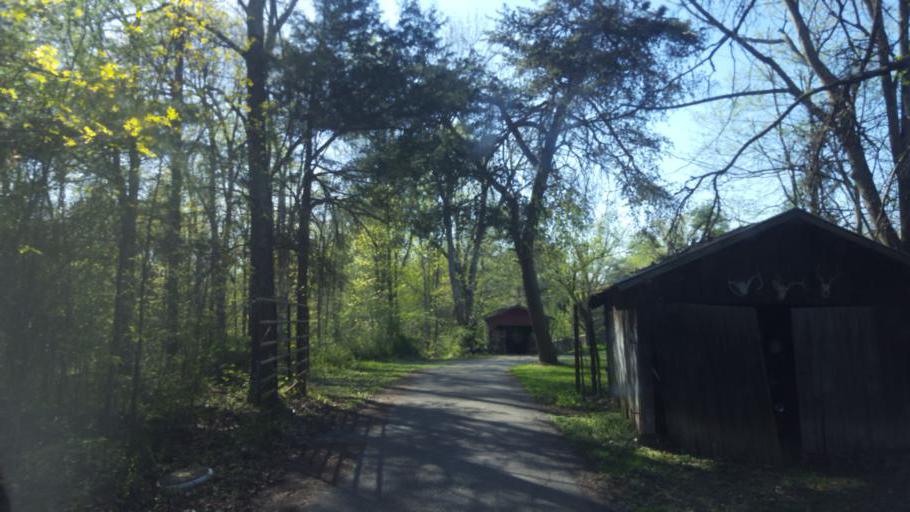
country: US
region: Kentucky
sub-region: Barren County
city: Cave City
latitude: 37.1765
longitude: -86.0330
